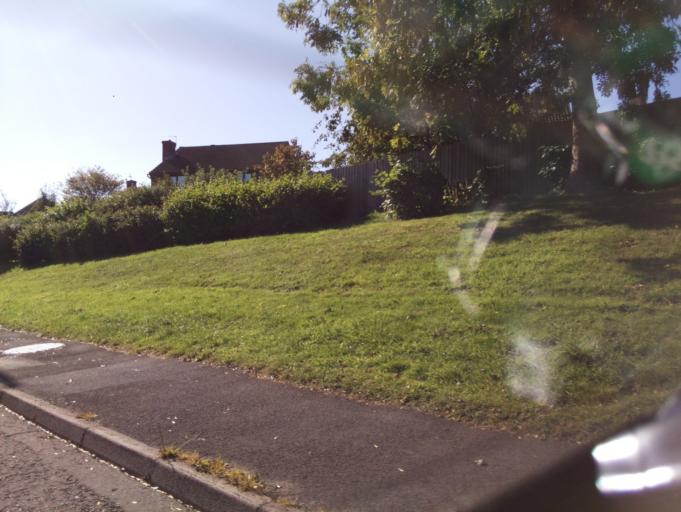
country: GB
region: Wales
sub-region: Torfaen County Borough
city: Cwmbran
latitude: 51.6382
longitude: -3.0590
